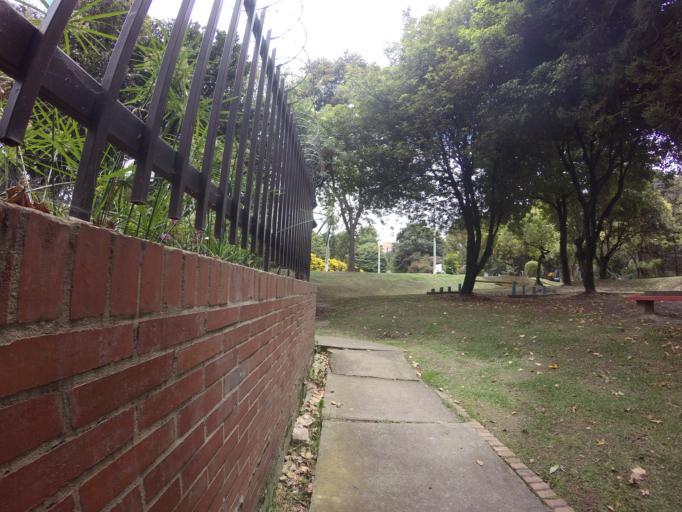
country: CO
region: Bogota D.C.
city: Barrio San Luis
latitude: 4.7085
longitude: -74.0577
